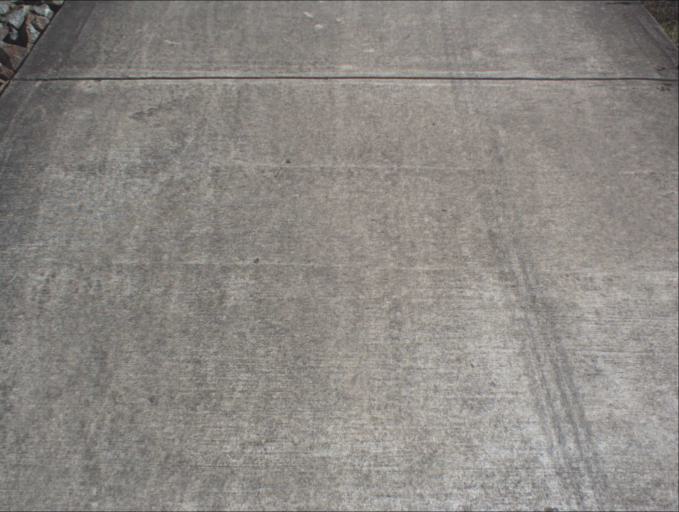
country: AU
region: Queensland
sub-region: Logan
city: Waterford West
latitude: -27.7092
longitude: 153.1612
